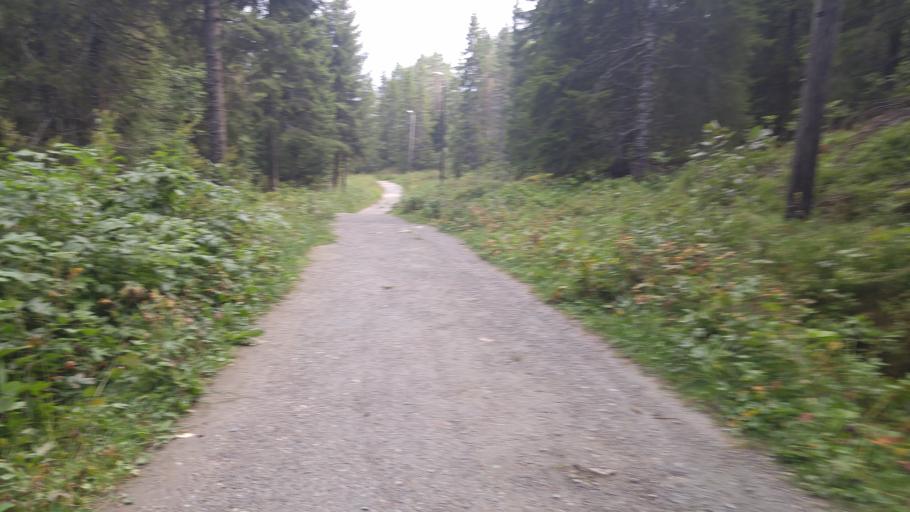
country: NO
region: Sor-Trondelag
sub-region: Trondheim
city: Trondheim
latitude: 63.4105
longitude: 10.3320
